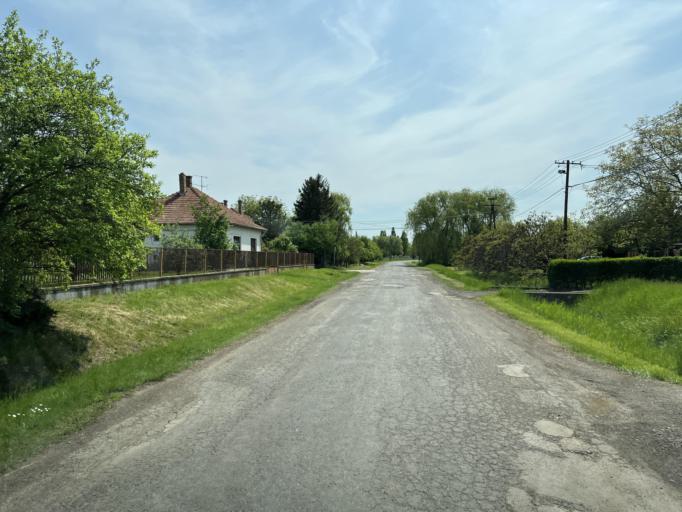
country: HU
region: Pest
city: Tapiogyorgye
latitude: 47.3377
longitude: 19.9559
